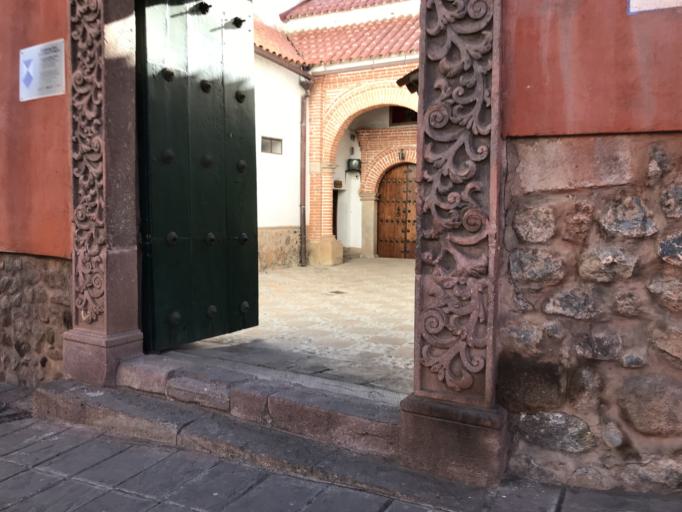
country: BO
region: Potosi
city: Potosi
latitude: -19.5890
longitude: -65.7568
